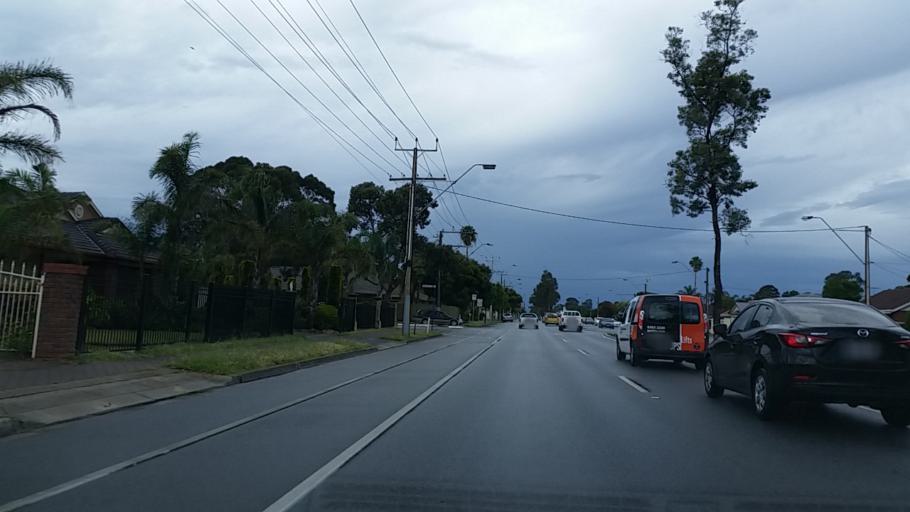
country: AU
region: South Australia
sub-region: Salisbury
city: Salisbury
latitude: -34.7948
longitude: 138.6123
